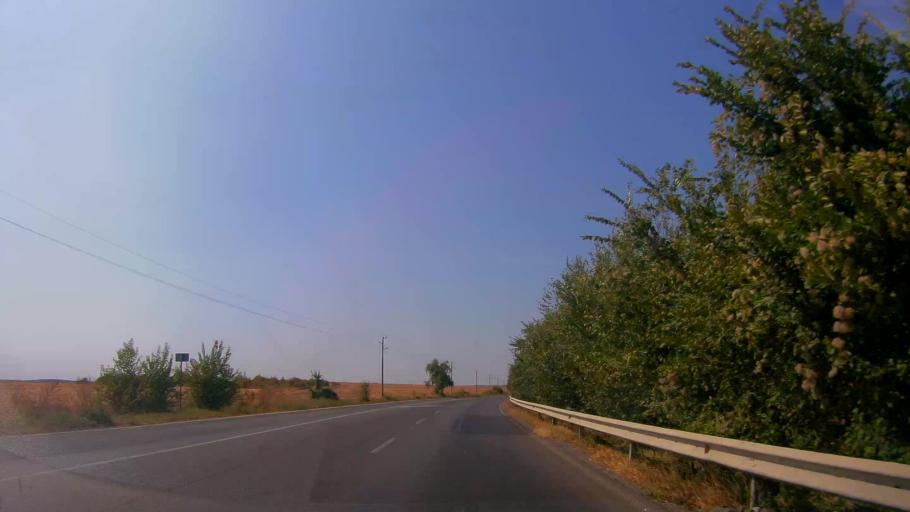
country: BG
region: Ruse
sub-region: Obshtina Vetovo
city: Senovo
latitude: 43.5619
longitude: 26.3558
